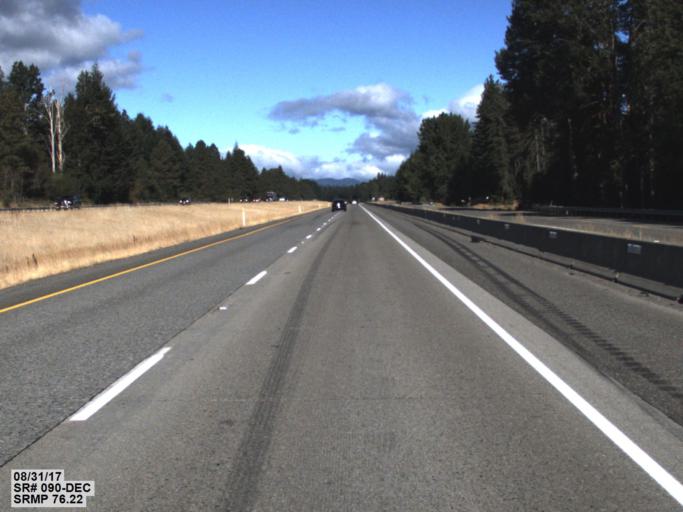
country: US
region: Washington
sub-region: Kittitas County
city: Cle Elum
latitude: 47.2069
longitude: -121.0877
